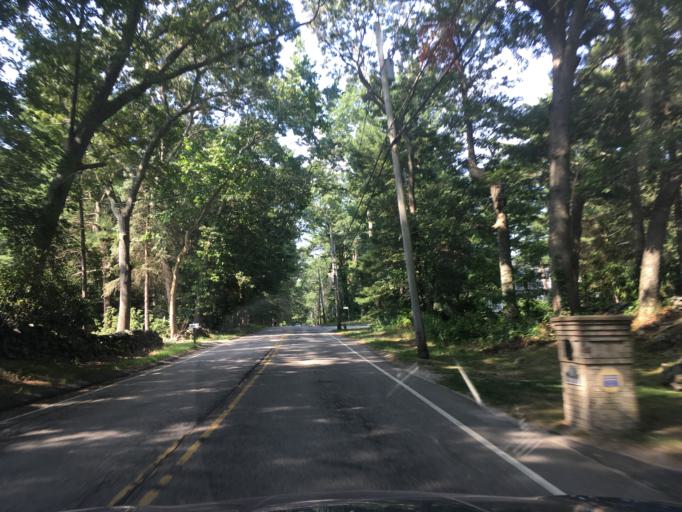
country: US
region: Rhode Island
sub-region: Kent County
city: East Greenwich
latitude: 41.6221
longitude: -71.4317
